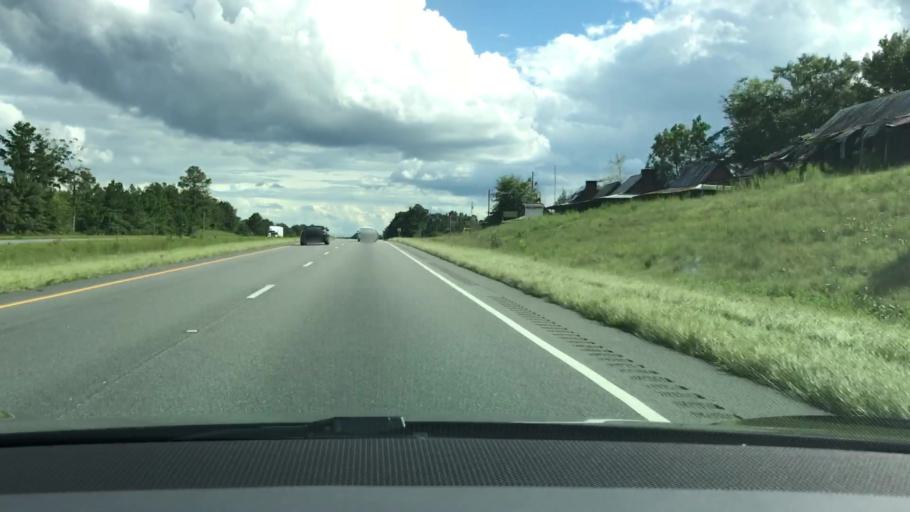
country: US
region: Alabama
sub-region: Pike County
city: Troy
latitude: 31.9030
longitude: -86.0113
